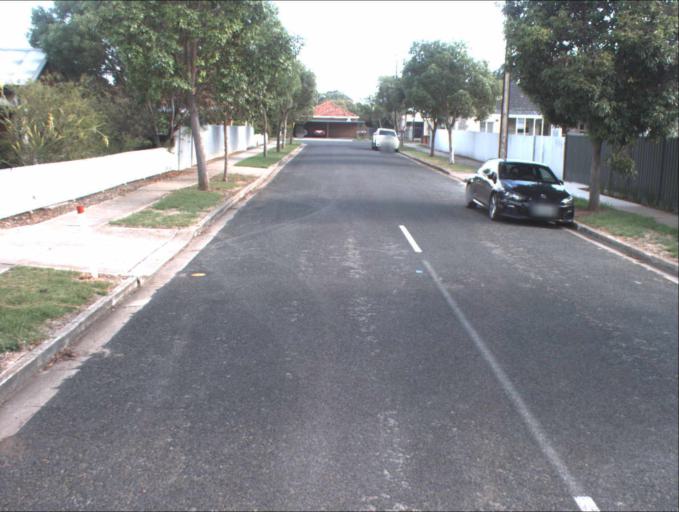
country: AU
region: South Australia
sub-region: Port Adelaide Enfield
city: Klemzig
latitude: -34.8766
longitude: 138.6221
